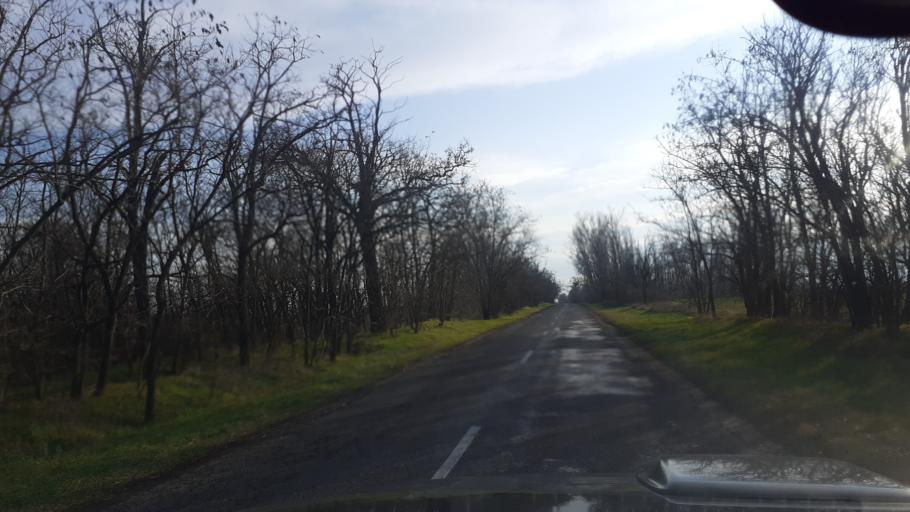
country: HU
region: Bacs-Kiskun
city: Kunszentmiklos
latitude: 47.0977
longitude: 19.0925
